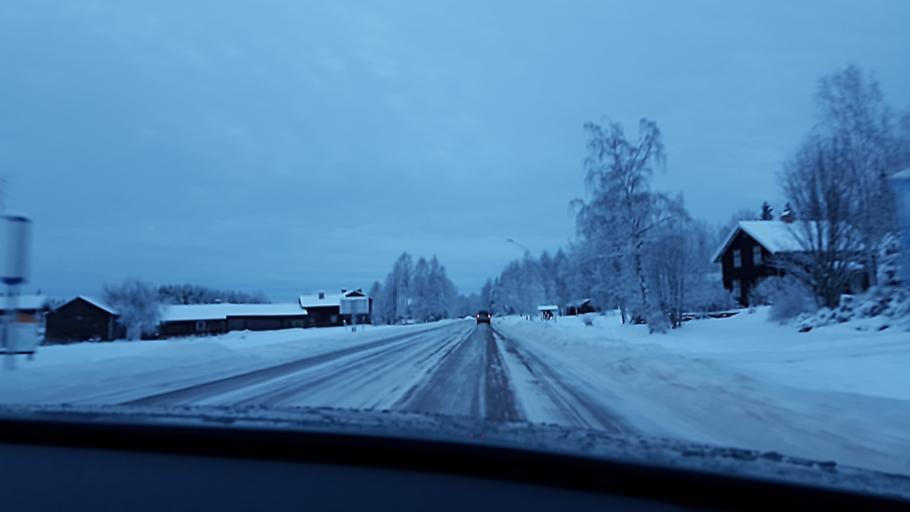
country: SE
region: Jaemtland
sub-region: Harjedalens Kommun
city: Sveg
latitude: 62.0487
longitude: 14.6481
